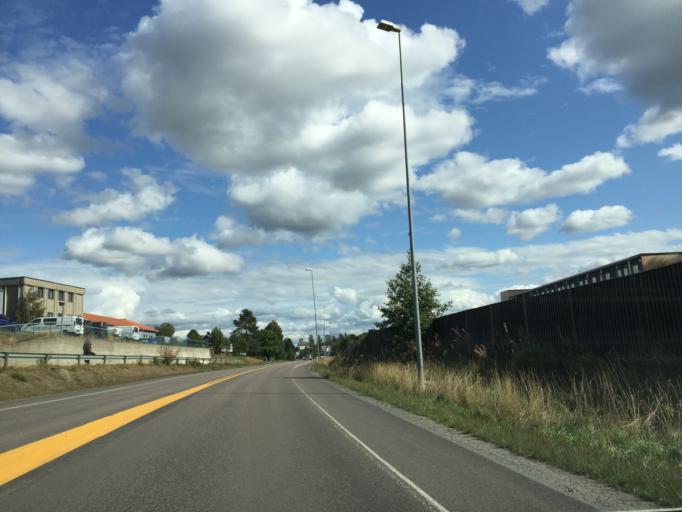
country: NO
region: Ostfold
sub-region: Hobol
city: Knappstad
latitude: 59.6169
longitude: 11.0578
